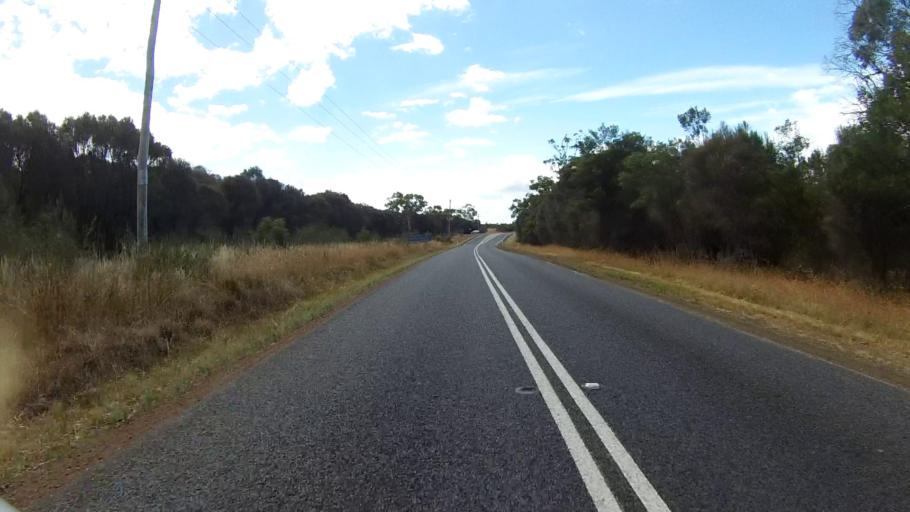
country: AU
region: Tasmania
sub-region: Sorell
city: Sorell
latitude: -42.1449
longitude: 148.0680
